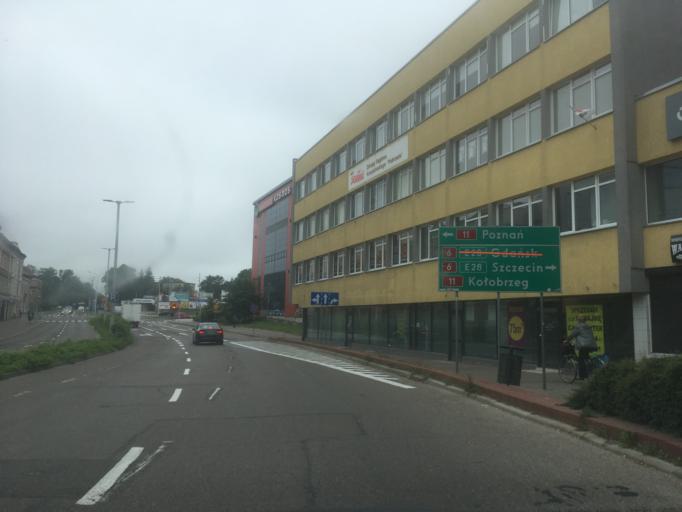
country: PL
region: West Pomeranian Voivodeship
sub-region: Koszalin
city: Koszalin
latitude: 54.1900
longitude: 16.1739
